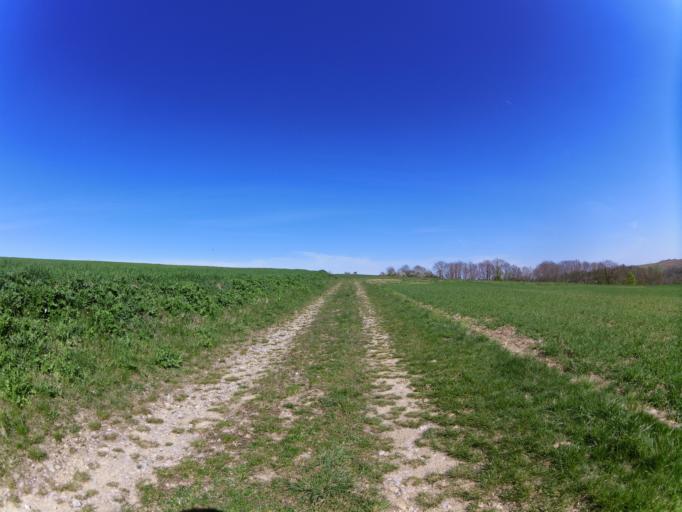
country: DE
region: Bavaria
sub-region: Regierungsbezirk Unterfranken
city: Winterhausen
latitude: 49.6790
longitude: 10.0005
